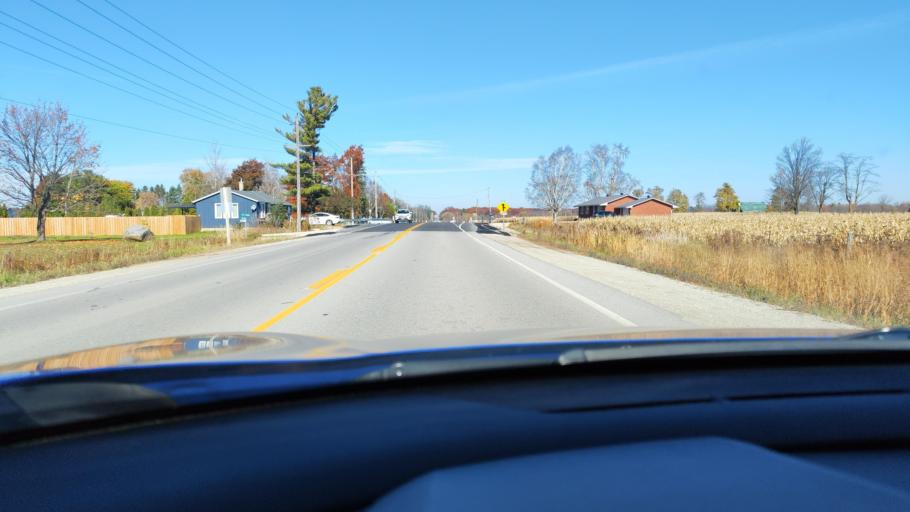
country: CA
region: Ontario
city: Wasaga Beach
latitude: 44.4543
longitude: -80.0714
